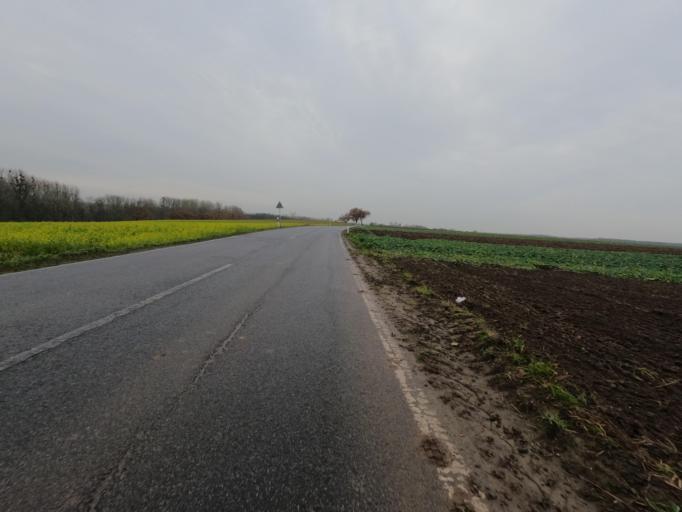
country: DE
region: North Rhine-Westphalia
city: Geilenkirchen
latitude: 51.0113
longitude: 6.1706
